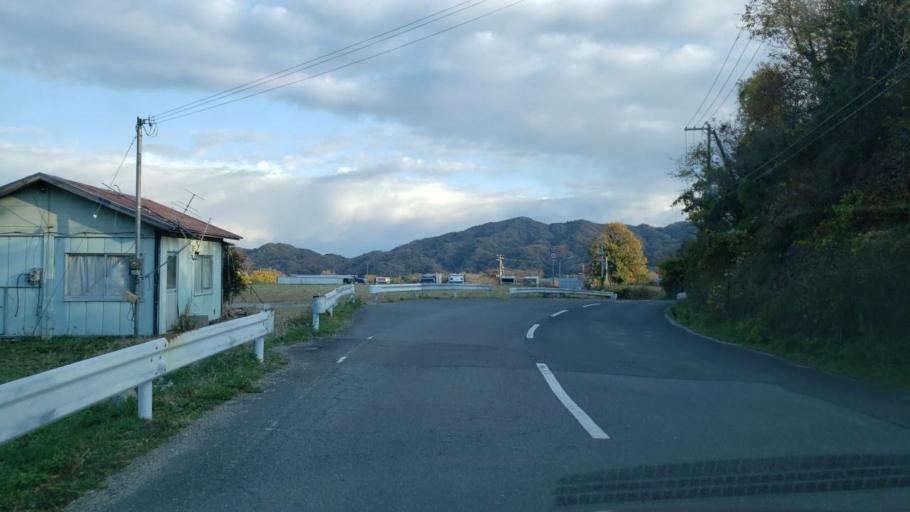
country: JP
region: Hyogo
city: Akashi
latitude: 34.5314
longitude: 134.9488
